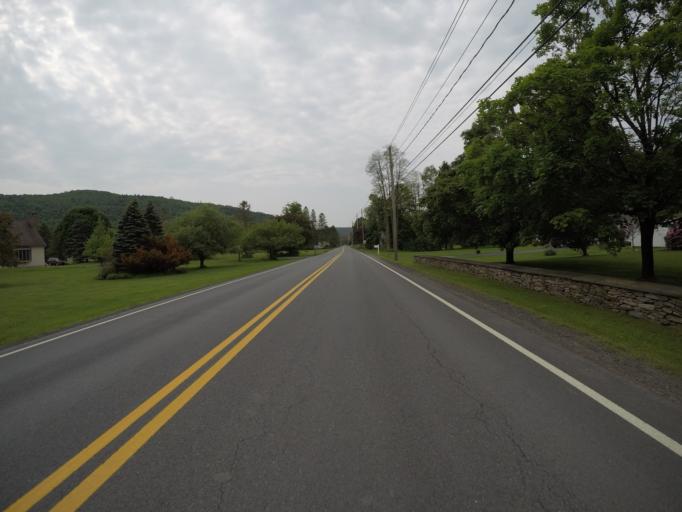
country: US
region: New York
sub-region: Sullivan County
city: Livingston Manor
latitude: 41.9545
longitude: -74.9092
